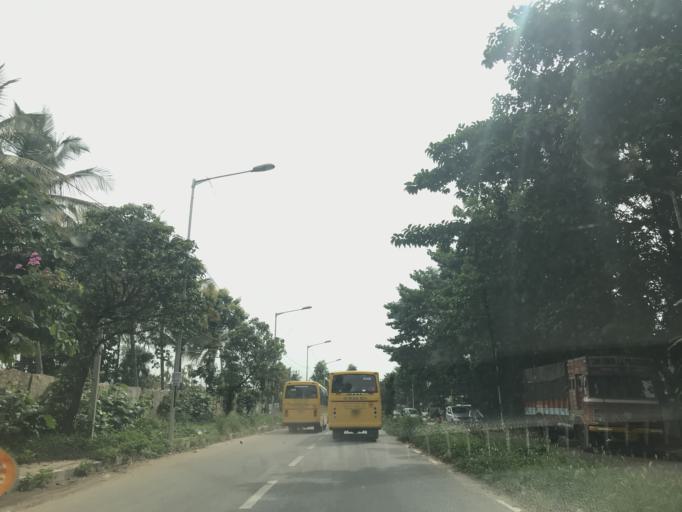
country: IN
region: Karnataka
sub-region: Bangalore Urban
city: Yelahanka
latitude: 13.1225
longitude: 77.6335
